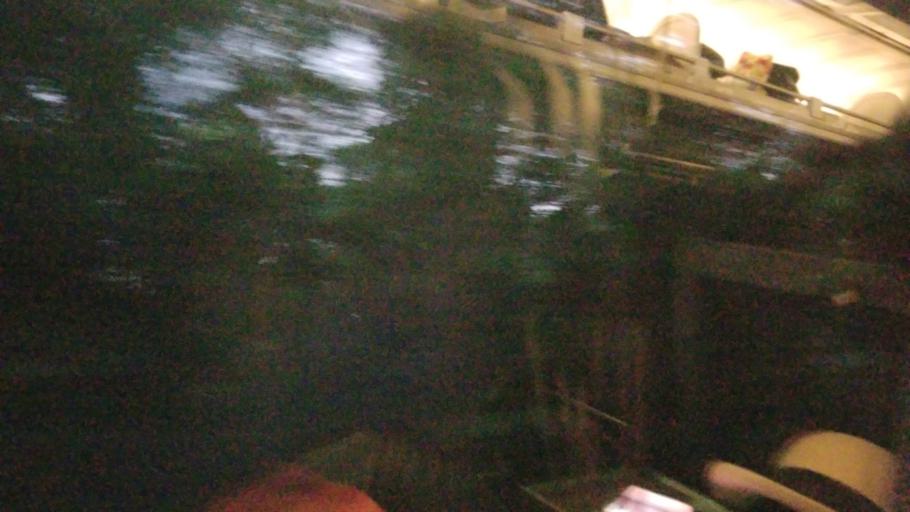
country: US
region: Virginia
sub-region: Orange County
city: Gordonsville
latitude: 38.1866
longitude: -78.2505
